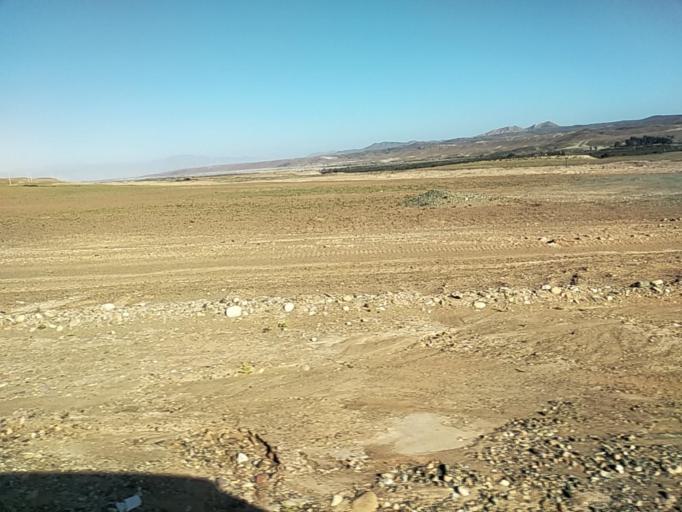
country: CL
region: Atacama
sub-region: Provincia de Copiapo
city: Copiapo
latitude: -27.3302
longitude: -70.7834
